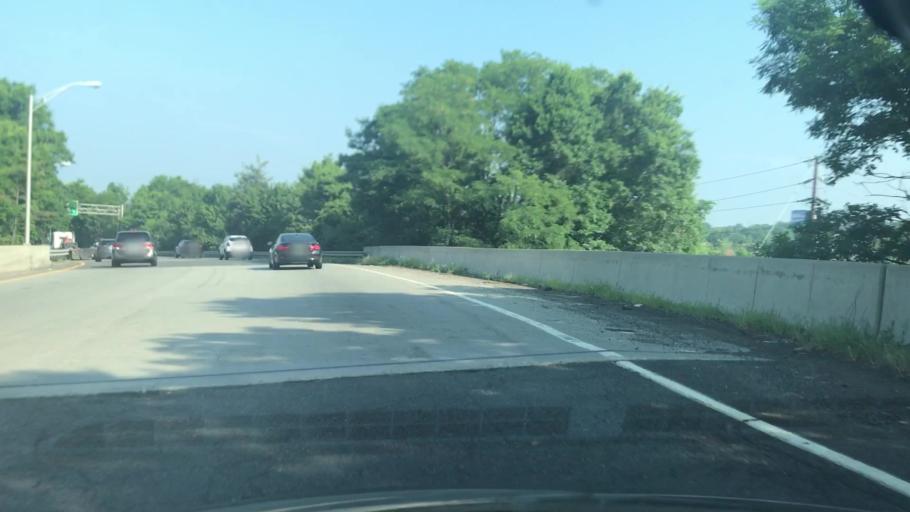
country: US
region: New Jersey
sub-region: Middlesex County
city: Fords
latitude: 40.5279
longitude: -74.3299
